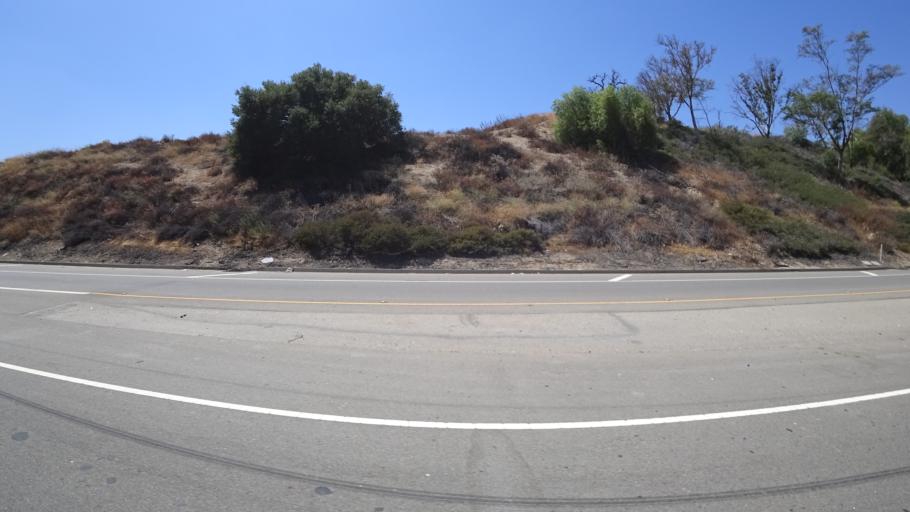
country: US
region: California
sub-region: Los Angeles County
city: Santa Clarita
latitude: 34.3922
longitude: -118.5710
